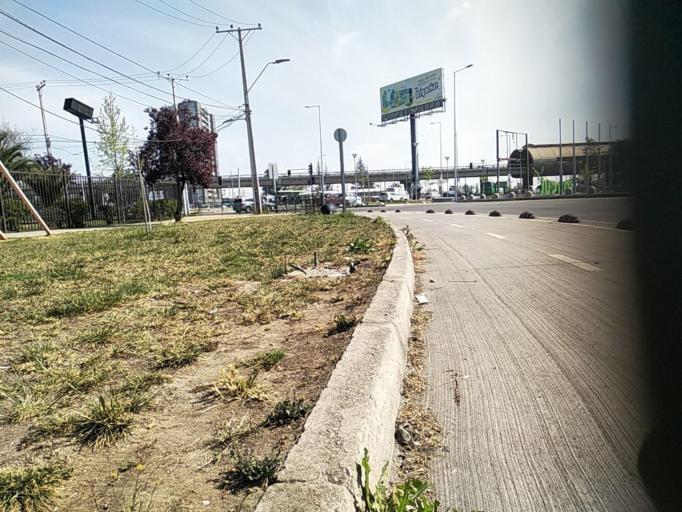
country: CL
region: Santiago Metropolitan
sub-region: Provincia de Santiago
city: Villa Presidente Frei, Nunoa, Santiago, Chile
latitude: -33.5079
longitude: -70.6103
